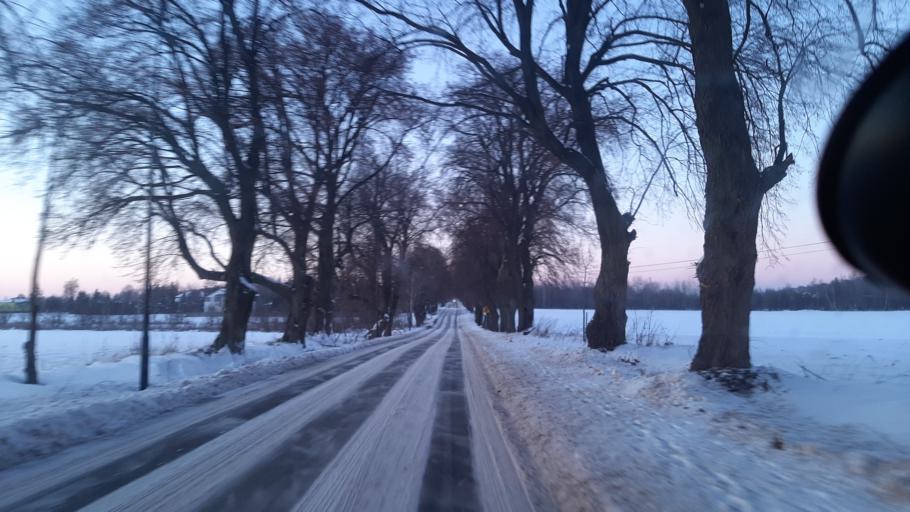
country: PL
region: Lublin Voivodeship
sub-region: Powiat lubelski
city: Lublin
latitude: 51.3279
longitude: 22.5582
